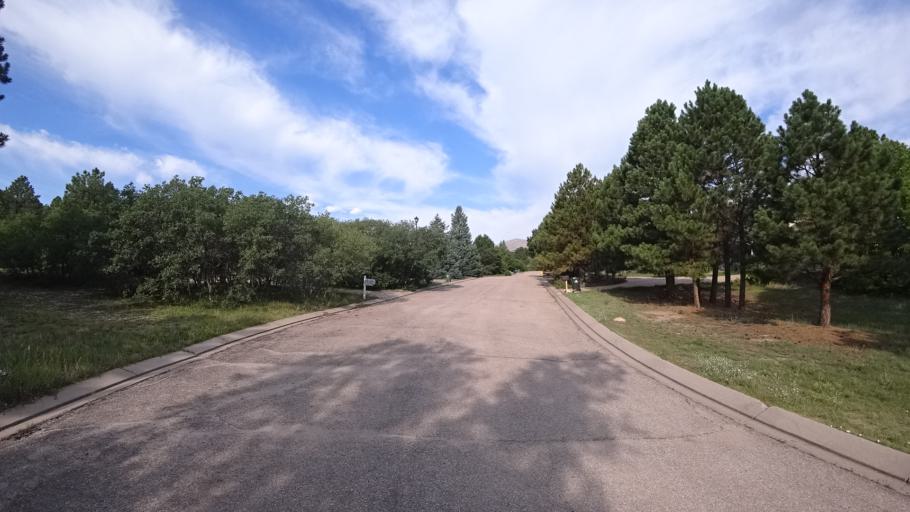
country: US
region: Colorado
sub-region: El Paso County
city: Air Force Academy
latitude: 38.9374
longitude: -104.8245
